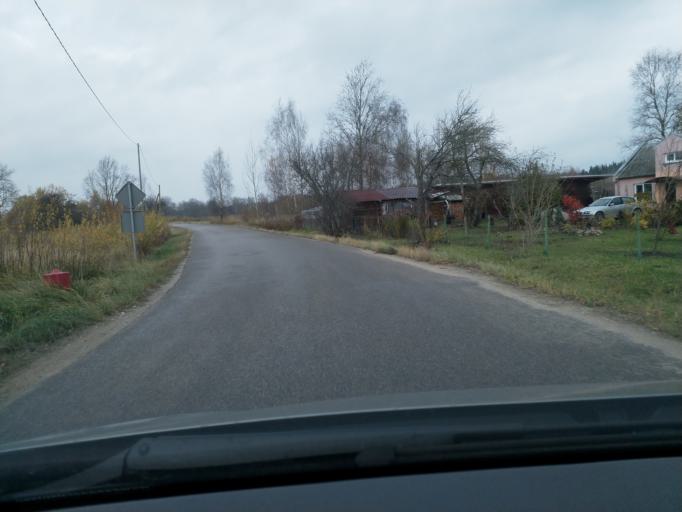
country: LV
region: Kuldigas Rajons
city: Kuldiga
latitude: 56.9772
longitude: 21.9788
